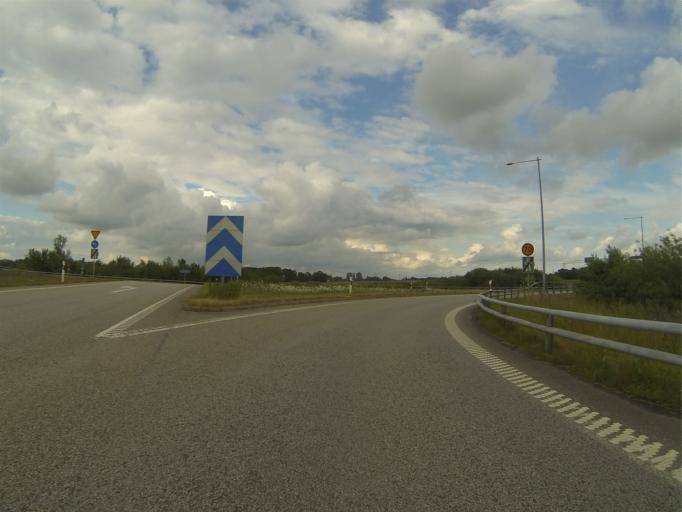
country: SE
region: Skane
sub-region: Burlovs Kommun
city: Arloev
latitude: 55.6412
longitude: 13.1071
